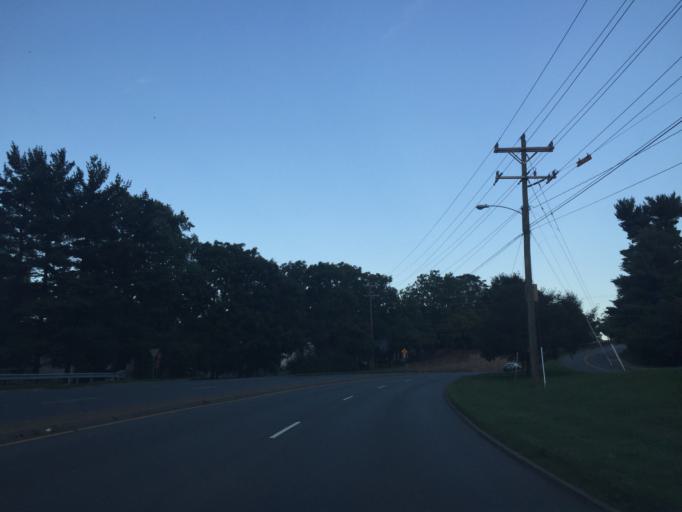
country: US
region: Virginia
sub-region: City of Charlottesville
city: Charlottesville
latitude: 38.0389
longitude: -78.4678
